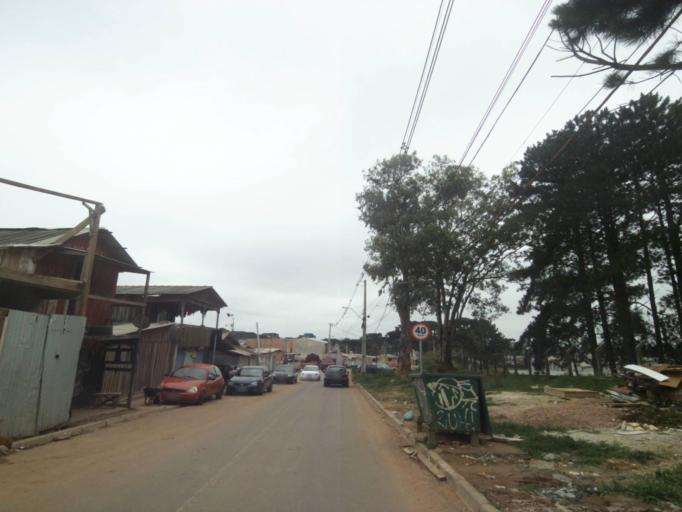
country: BR
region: Parana
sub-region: Araucaria
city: Araucaria
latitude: -25.5076
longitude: -49.3514
